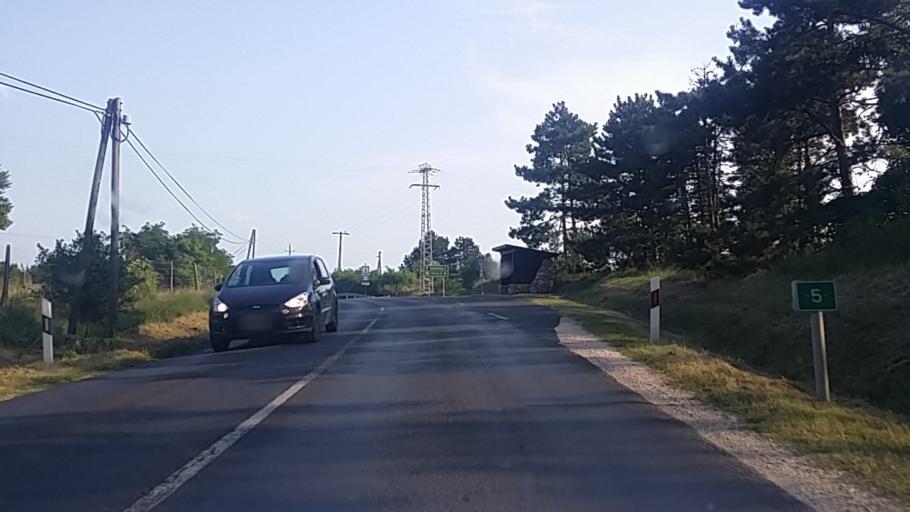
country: HU
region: Zala
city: Cserszegtomaj
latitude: 46.7988
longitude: 17.2068
